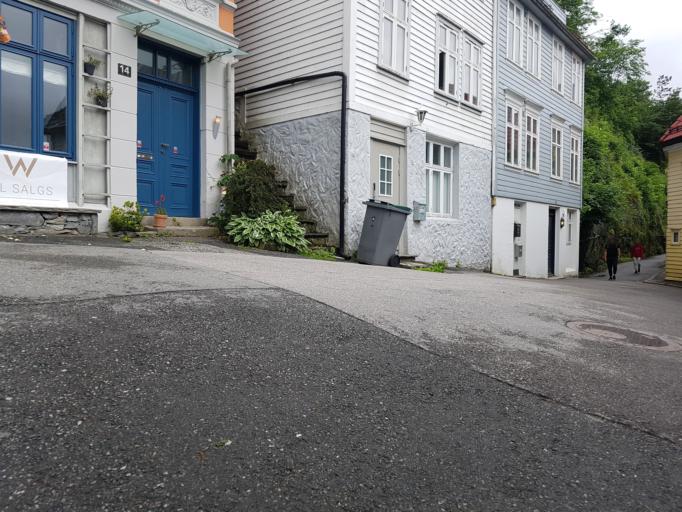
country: NO
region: Hordaland
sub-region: Bergen
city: Bergen
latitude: 60.3955
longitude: 5.3307
